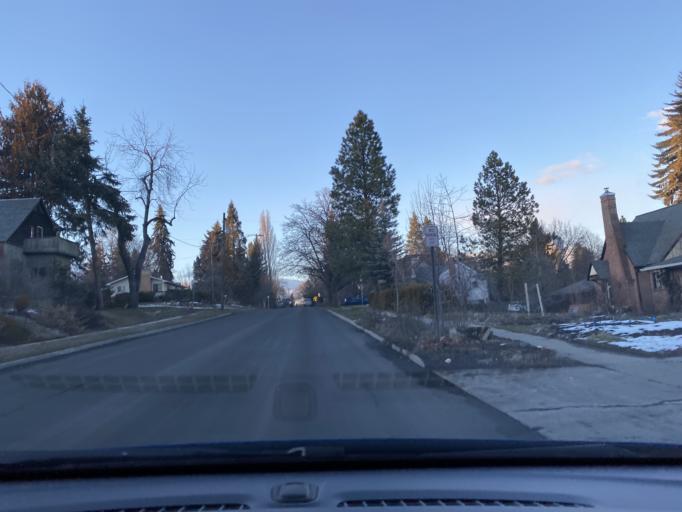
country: US
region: Idaho
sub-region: Latah County
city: Moscow
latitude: 46.7381
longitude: -116.9885
